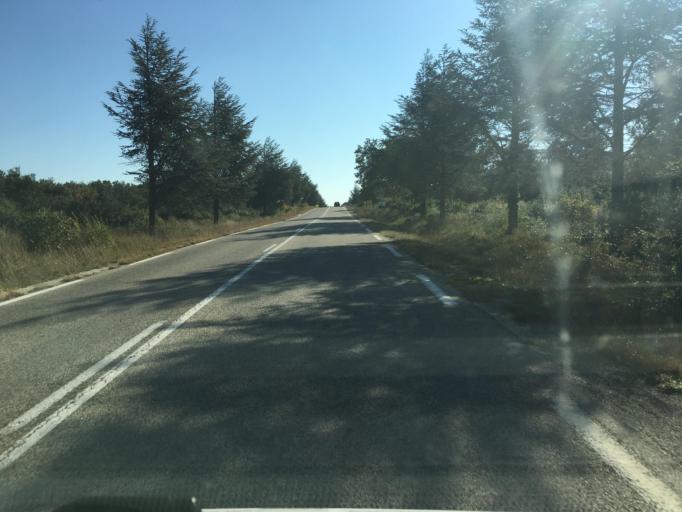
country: FR
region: Languedoc-Roussillon
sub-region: Departement du Gard
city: Saint-Quentin-la-Poterie
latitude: 44.1270
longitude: 4.4508
